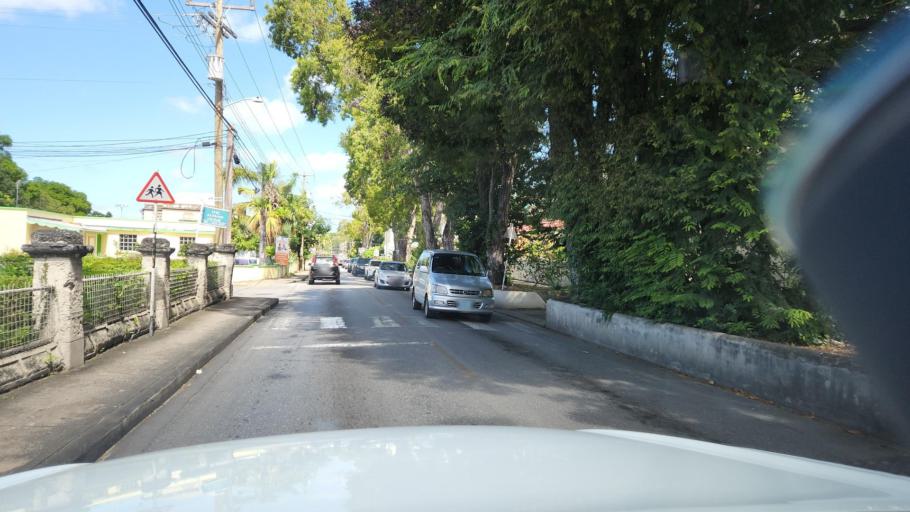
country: BB
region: Saint Michael
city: Bridgetown
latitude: 13.0951
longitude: -59.6016
